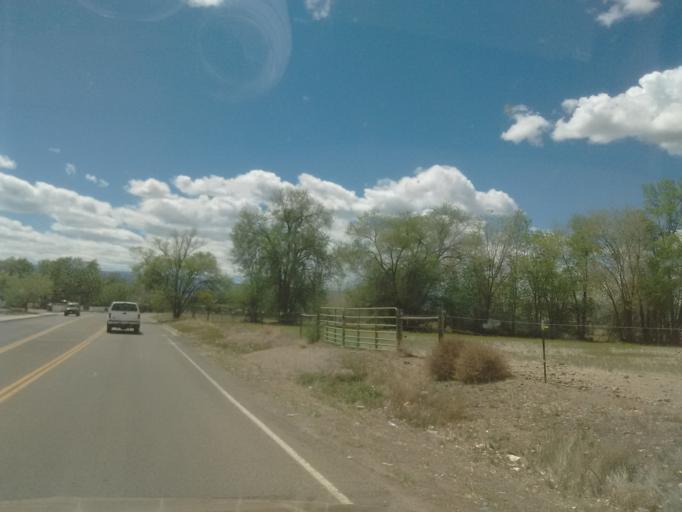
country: US
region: Colorado
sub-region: Mesa County
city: Fruitvale
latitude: 39.0766
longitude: -108.4937
